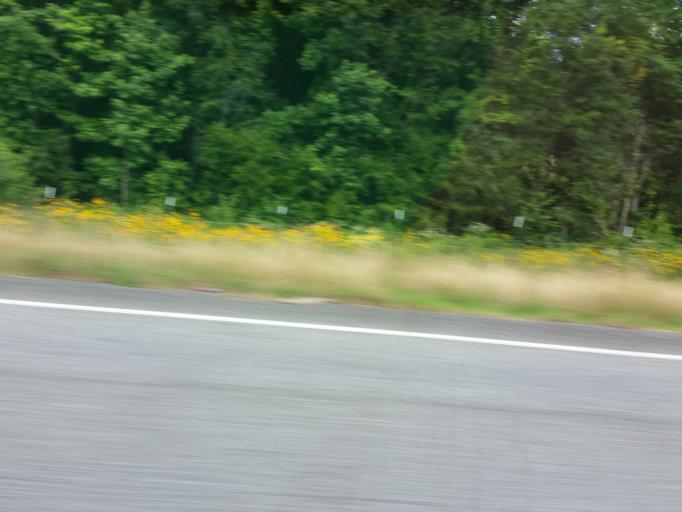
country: US
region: Alabama
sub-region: Sumter County
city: York
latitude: 32.3944
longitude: -88.2063
